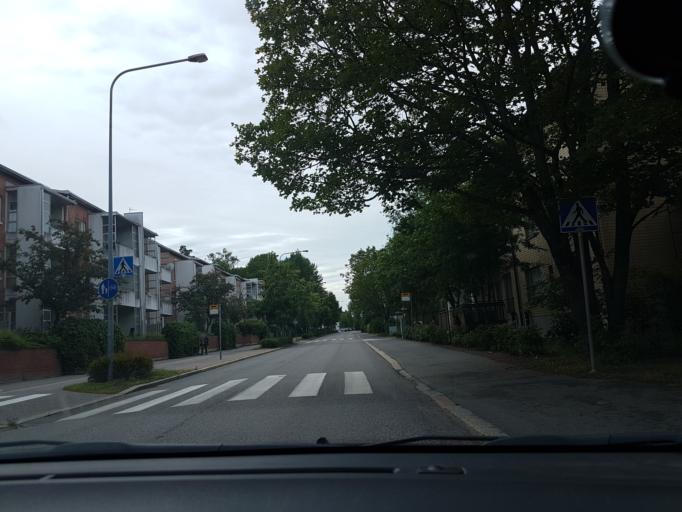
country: FI
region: Uusimaa
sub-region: Helsinki
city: Vantaa
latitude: 60.2558
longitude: 25.0104
